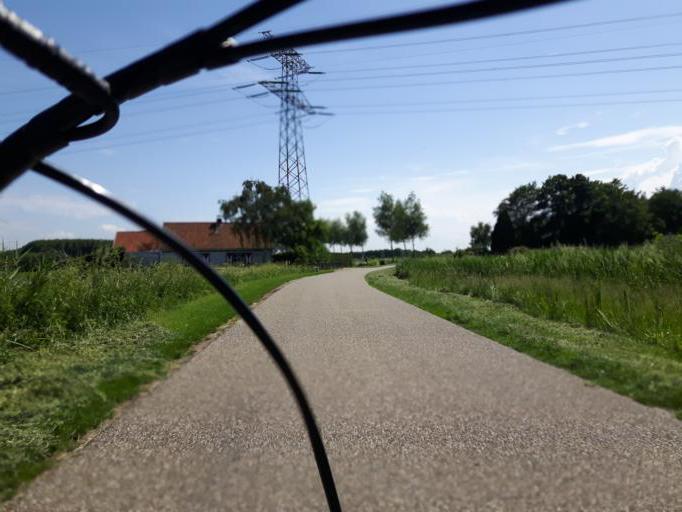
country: NL
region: Zeeland
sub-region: Gemeente Reimerswaal
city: Yerseke
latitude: 51.4596
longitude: 3.9945
